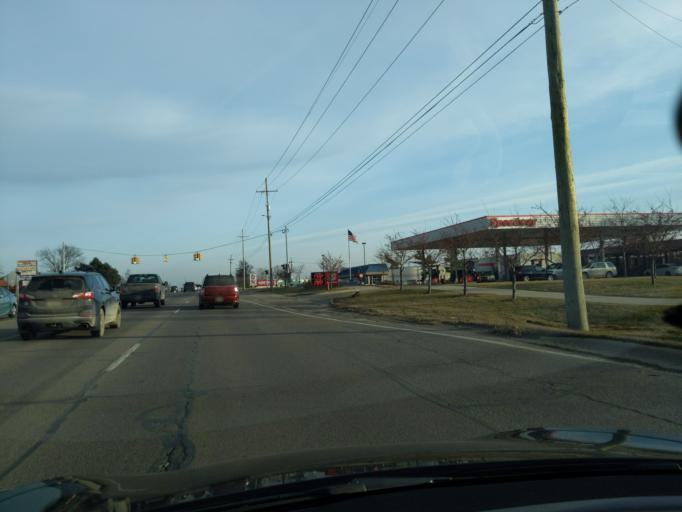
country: US
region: Michigan
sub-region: Livingston County
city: Howell
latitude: 42.5898
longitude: -83.8826
